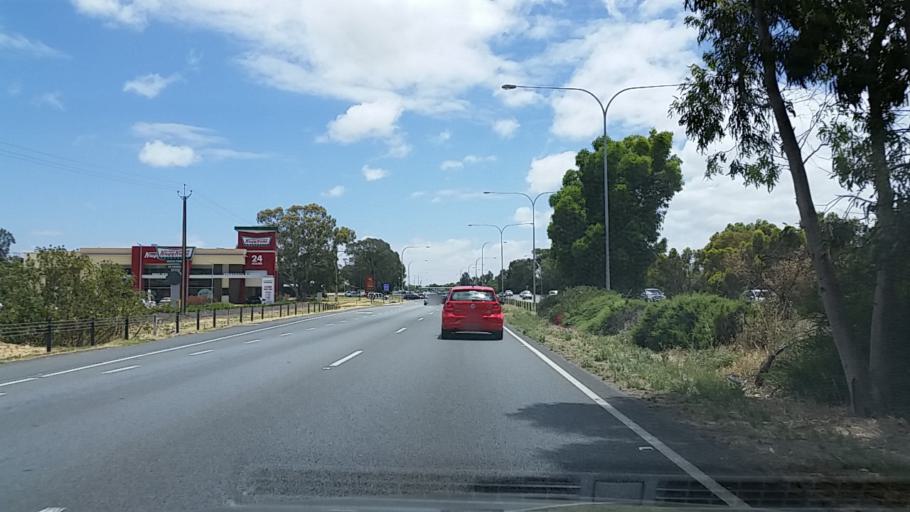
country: AU
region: South Australia
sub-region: Salisbury
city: Salisbury
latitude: -34.7689
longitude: 138.5942
